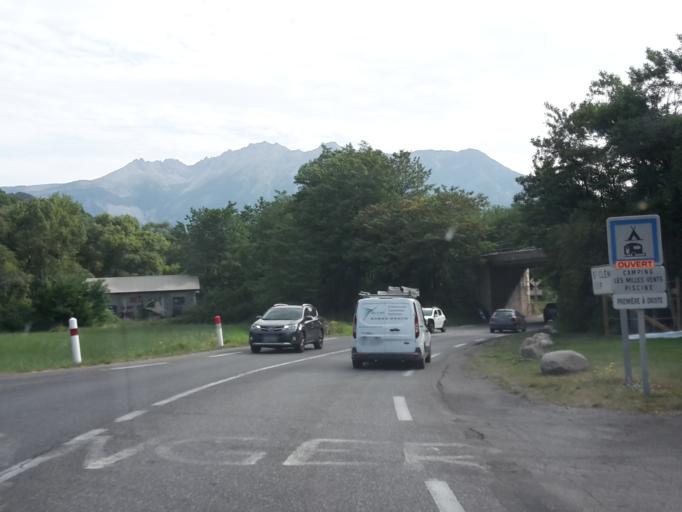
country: FR
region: Provence-Alpes-Cote d'Azur
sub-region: Departement des Hautes-Alpes
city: Guillestre
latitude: 44.6499
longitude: 6.5807
